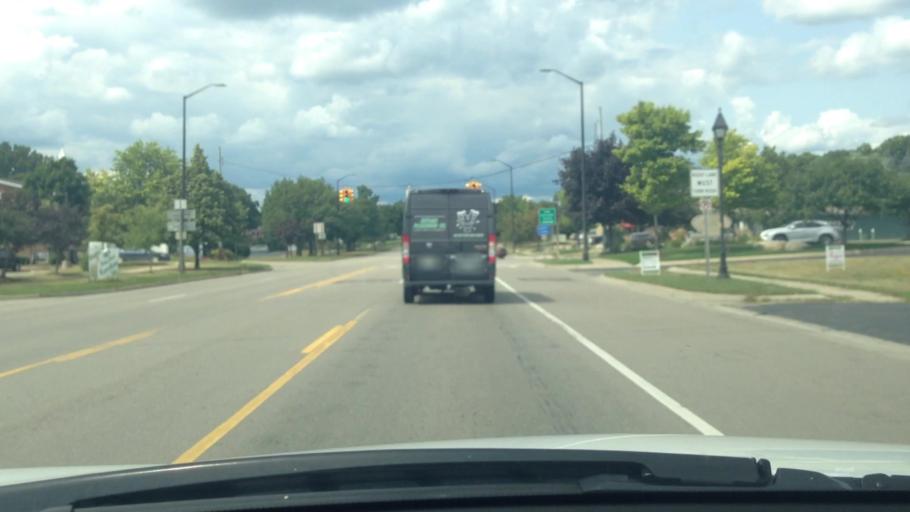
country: US
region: Michigan
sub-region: Oakland County
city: Clarkston
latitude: 42.7223
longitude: -83.4186
